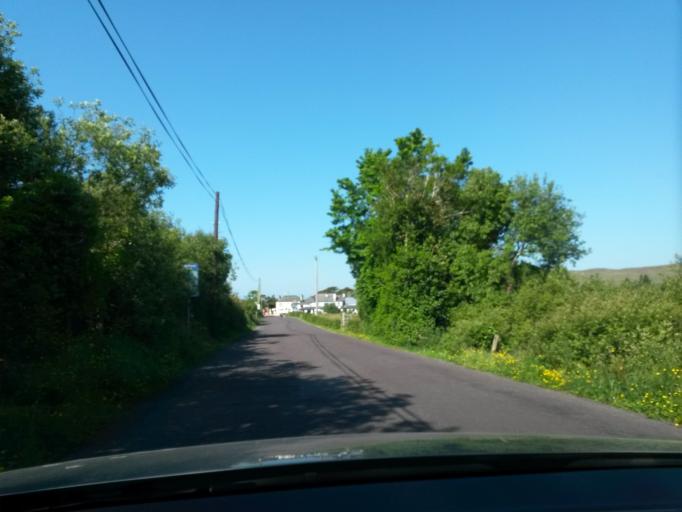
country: IE
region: Munster
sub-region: Ciarrai
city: Kenmare
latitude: 51.7355
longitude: -9.8934
